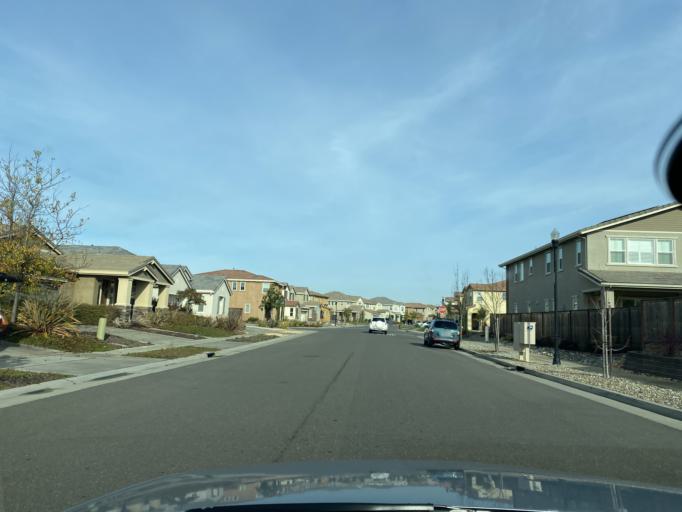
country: US
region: California
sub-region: Sacramento County
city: Elk Grove
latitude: 38.3970
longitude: -121.3923
